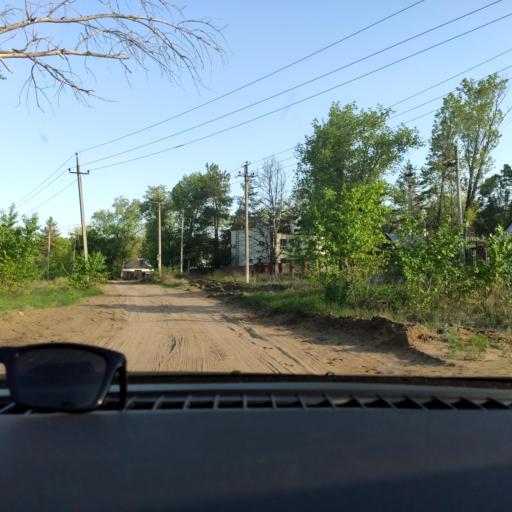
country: RU
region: Samara
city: Volzhskiy
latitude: 53.4336
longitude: 50.1619
